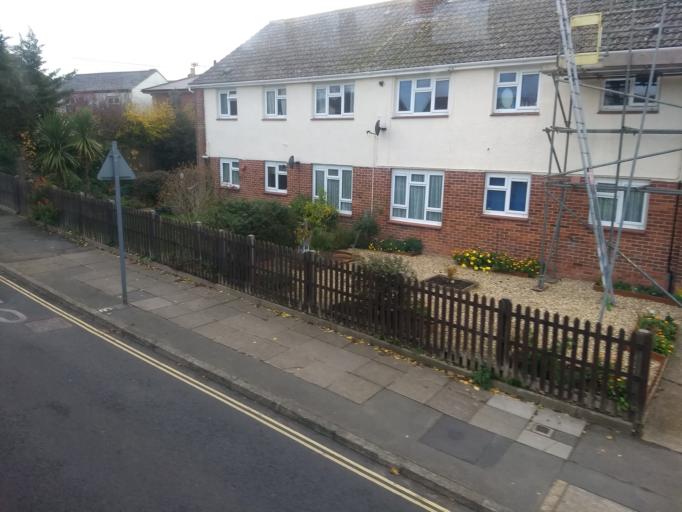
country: GB
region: England
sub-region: Isle of Wight
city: Newport
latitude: 50.6984
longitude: -1.3210
